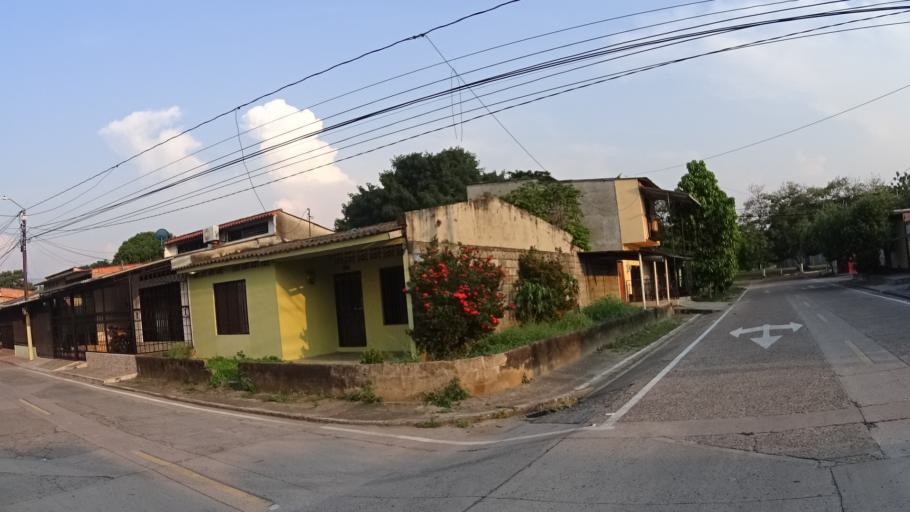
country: CO
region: Cundinamarca
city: Puerto Salgar
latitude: 5.4798
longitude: -74.6705
